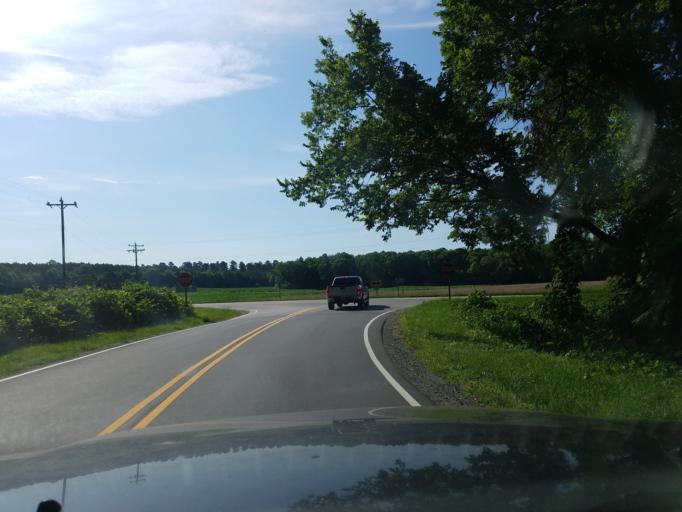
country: US
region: North Carolina
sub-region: Granville County
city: Butner
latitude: 36.1567
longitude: -78.7721
